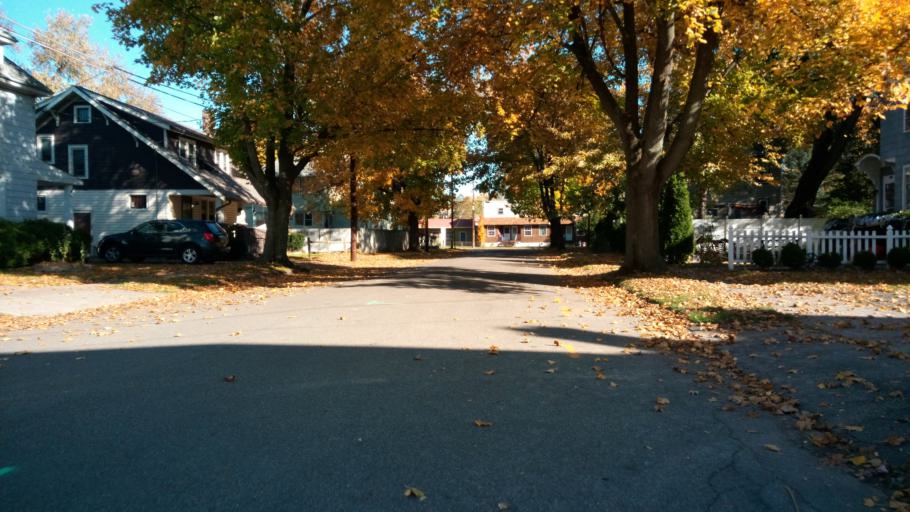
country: US
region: New York
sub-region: Chemung County
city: Elmira
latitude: 42.0726
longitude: -76.8063
